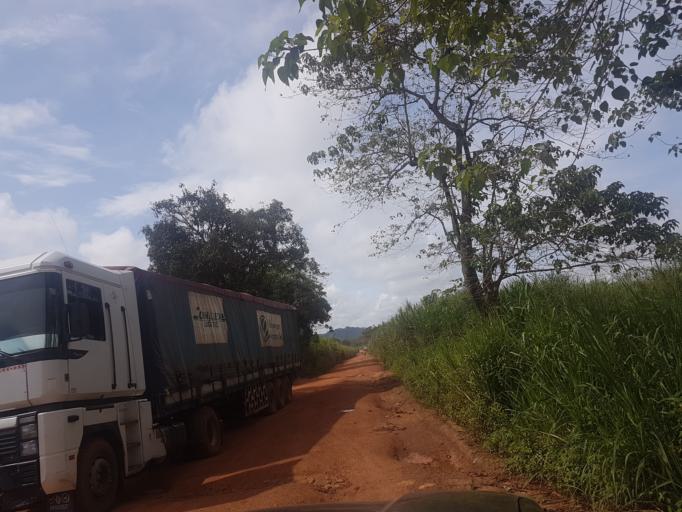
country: GN
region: Nzerekore
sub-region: Prefecture de Guekedou
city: Gueckedou
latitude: 8.6881
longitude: -10.1197
